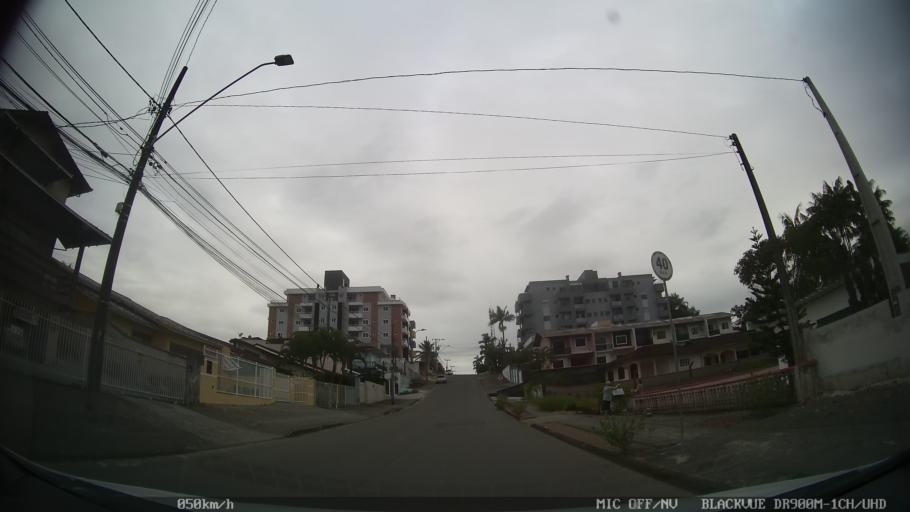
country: BR
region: Santa Catarina
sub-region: Joinville
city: Joinville
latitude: -26.2762
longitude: -48.8806
